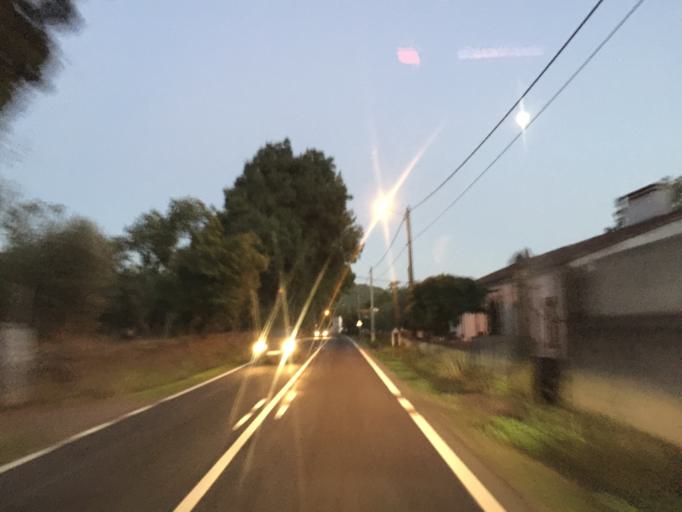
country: PT
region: Portalegre
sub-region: Marvao
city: Marvao
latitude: 39.3888
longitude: -7.4073
